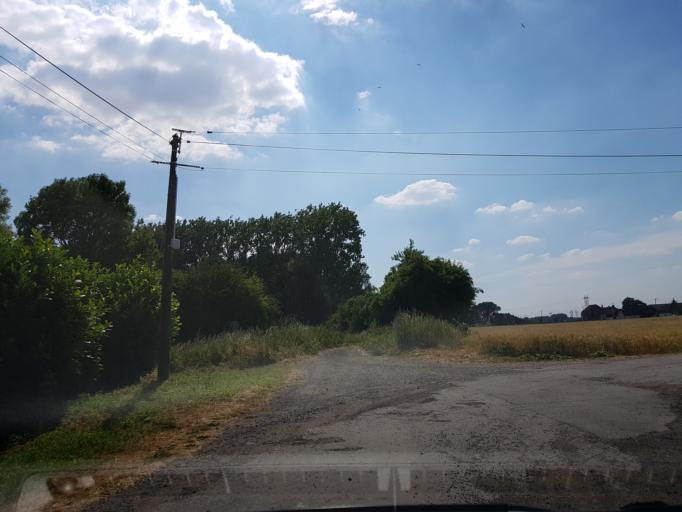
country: FR
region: Nord-Pas-de-Calais
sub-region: Departement du Nord
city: Roeulx
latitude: 50.3029
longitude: 3.3364
